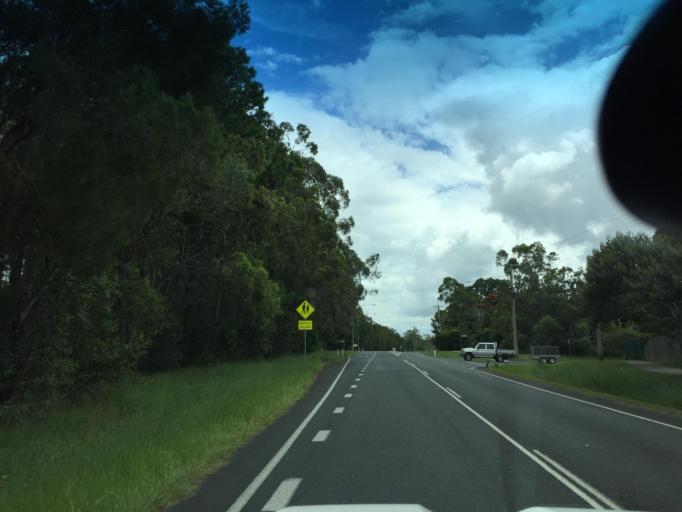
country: AU
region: Queensland
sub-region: Moreton Bay
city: Caboolture
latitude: -27.0458
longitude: 152.9351
